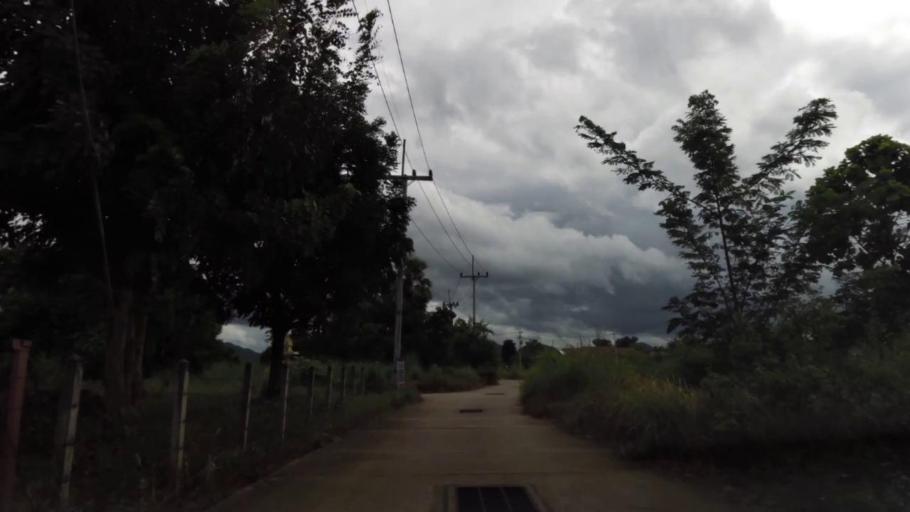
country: TH
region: Nakhon Sawan
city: Phai Sali
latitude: 15.5926
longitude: 100.6591
